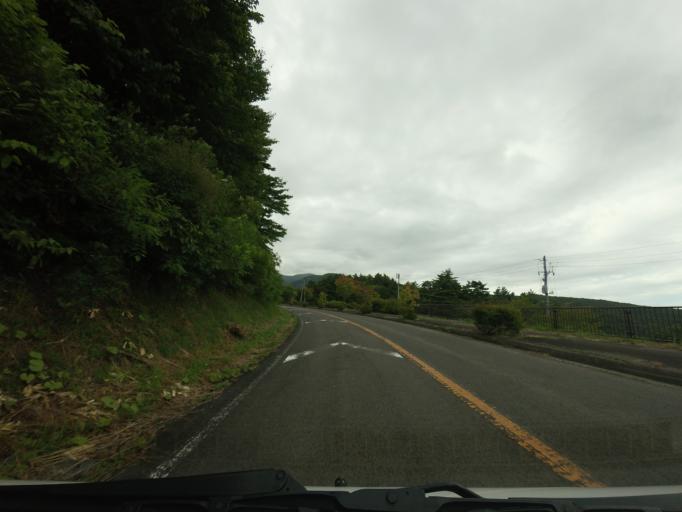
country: JP
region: Fukushima
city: Motomiya
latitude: 37.5817
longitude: 140.3352
